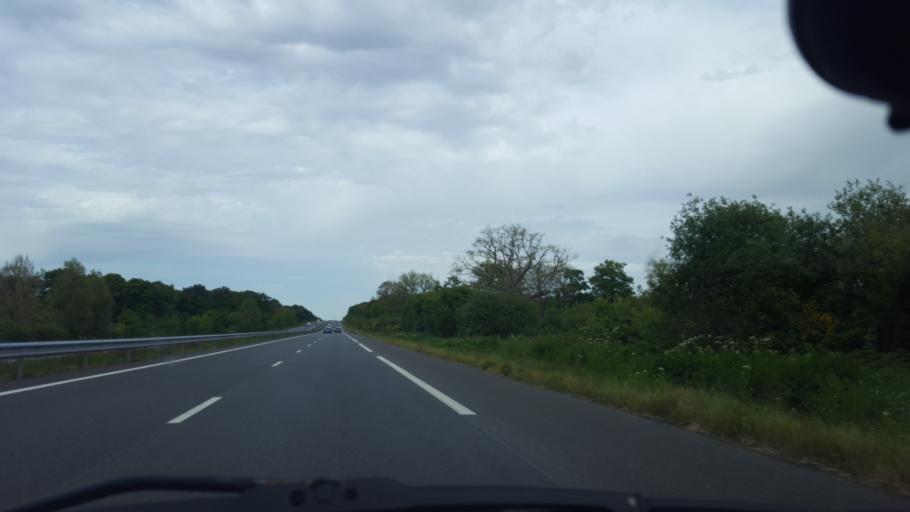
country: FR
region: Pays de la Loire
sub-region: Departement de la Loire-Atlantique
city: Saint-Lumine-de-Coutais
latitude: 47.0053
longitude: -1.7195
